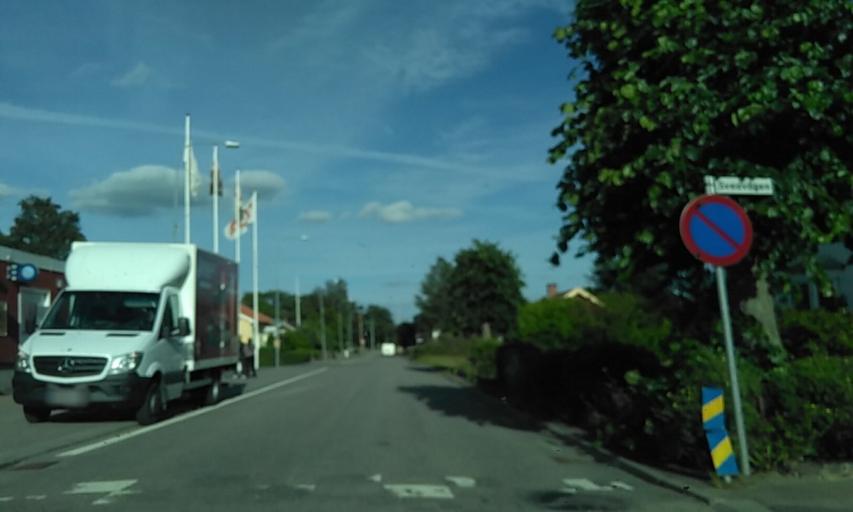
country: SE
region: Vaestra Goetaland
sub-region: Vara Kommun
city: Vara
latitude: 58.3254
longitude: 12.9216
